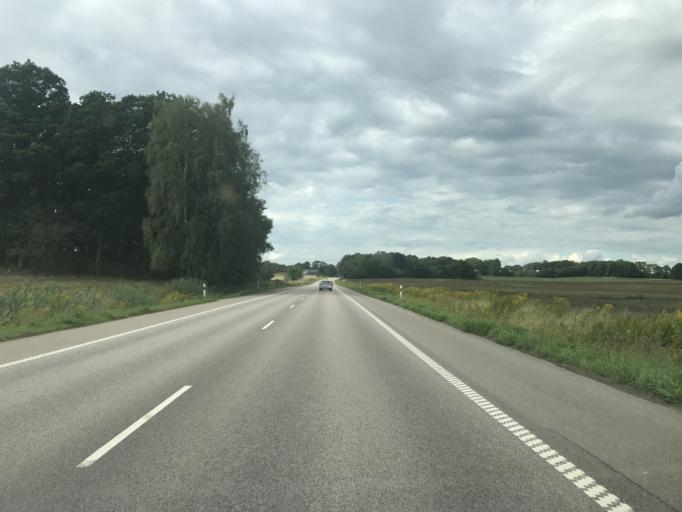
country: SE
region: Skane
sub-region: Hassleholms Kommun
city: Hassleholm
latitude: 56.1346
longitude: 13.8139
